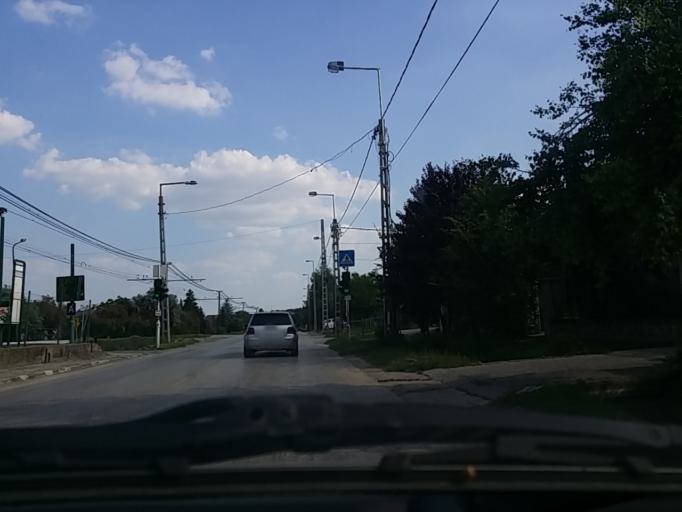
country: HU
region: Pest
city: Budakalasz
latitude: 47.6285
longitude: 19.0433
